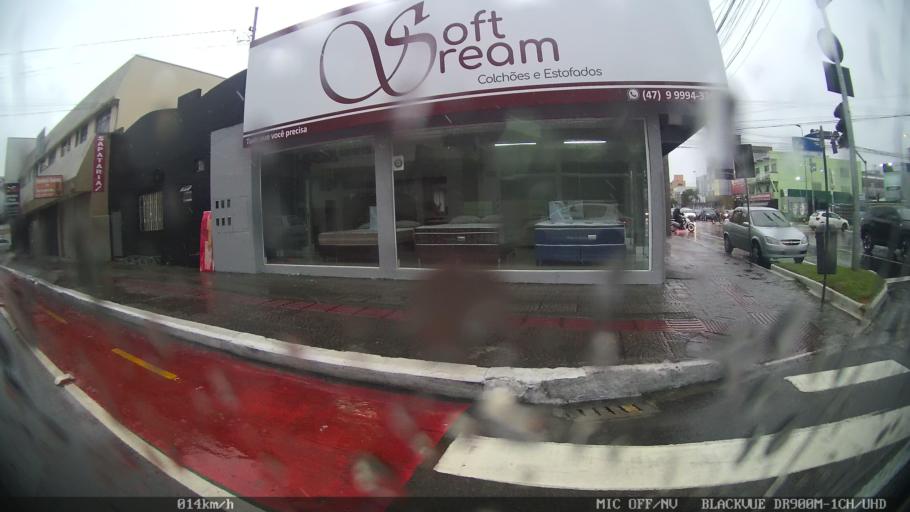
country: BR
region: Santa Catarina
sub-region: Balneario Camboriu
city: Balneario Camboriu
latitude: -27.0007
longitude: -48.6367
